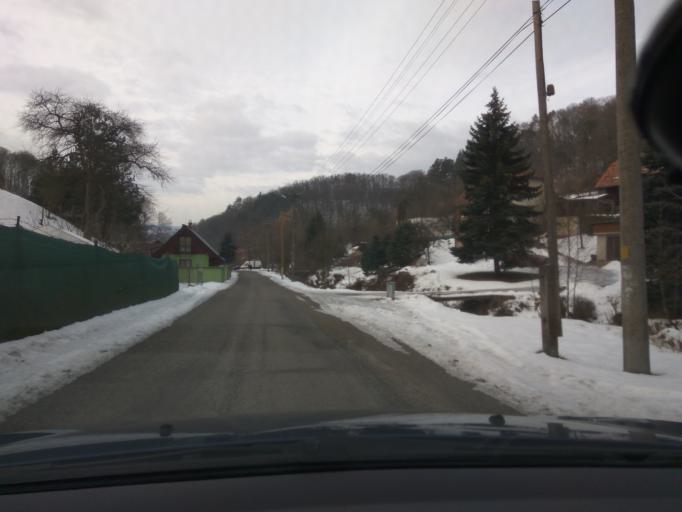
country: SK
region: Banskobystricky
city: Zarnovica
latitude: 48.4839
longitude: 18.7406
